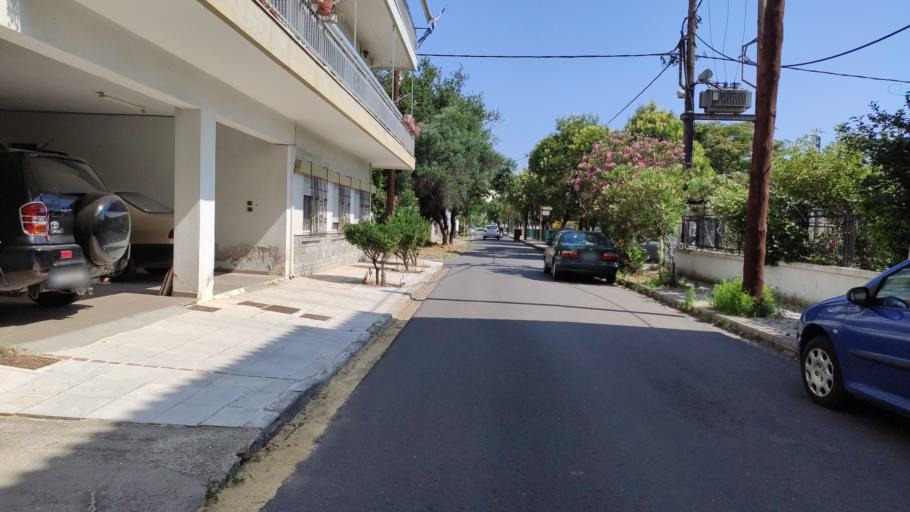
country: GR
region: East Macedonia and Thrace
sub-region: Nomos Rodopis
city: Komotini
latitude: 41.1128
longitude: 25.3933
